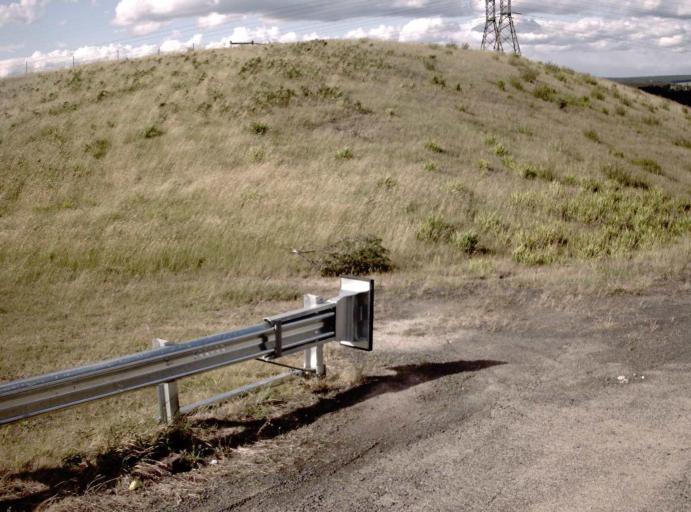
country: AU
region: Victoria
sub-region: Latrobe
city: Moe
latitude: -38.1814
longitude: 146.3310
